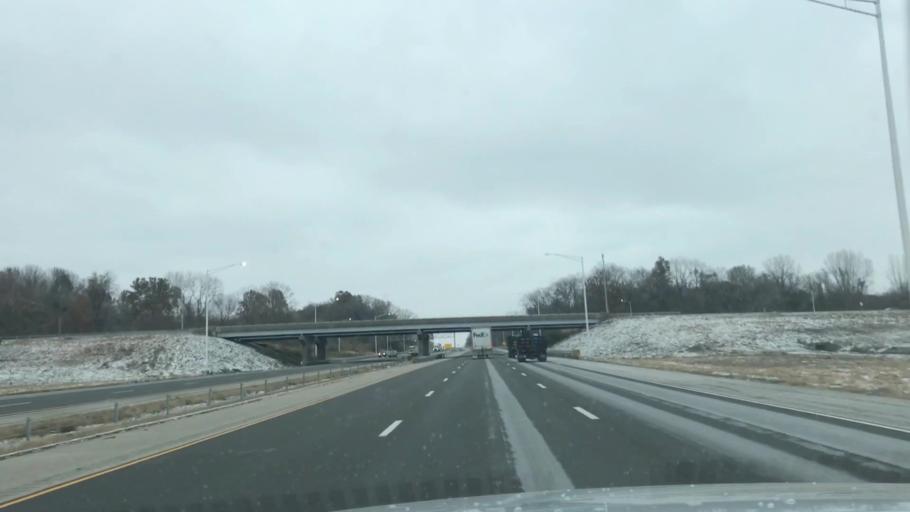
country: US
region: Illinois
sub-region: Madison County
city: Glen Carbon
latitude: 38.7565
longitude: -90.0095
